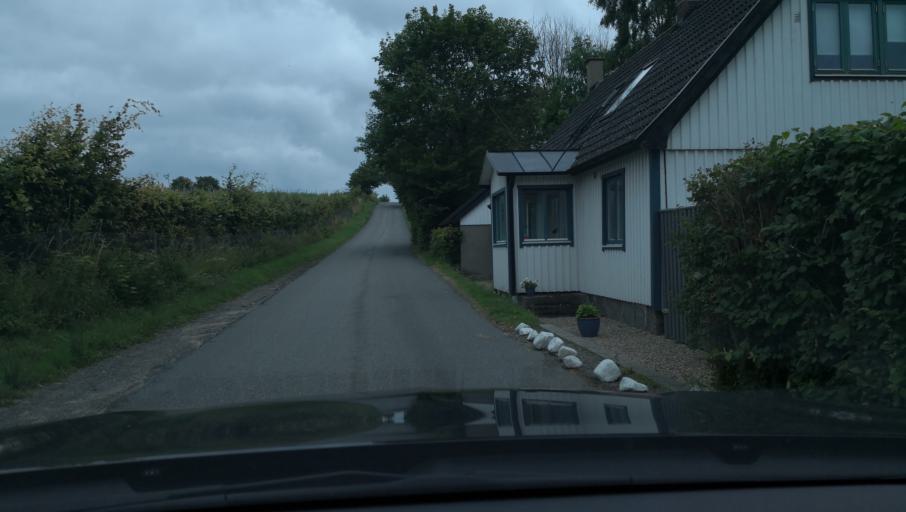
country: SE
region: Skane
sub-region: Simrishamns Kommun
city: Kivik
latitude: 55.7227
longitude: 14.1621
